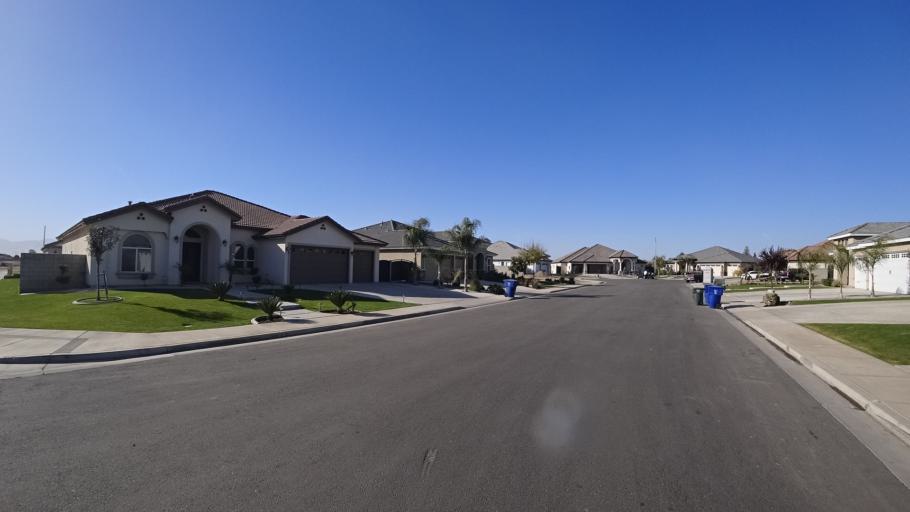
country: US
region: California
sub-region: Kern County
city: Greenfield
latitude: 35.2719
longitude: -119.0463
